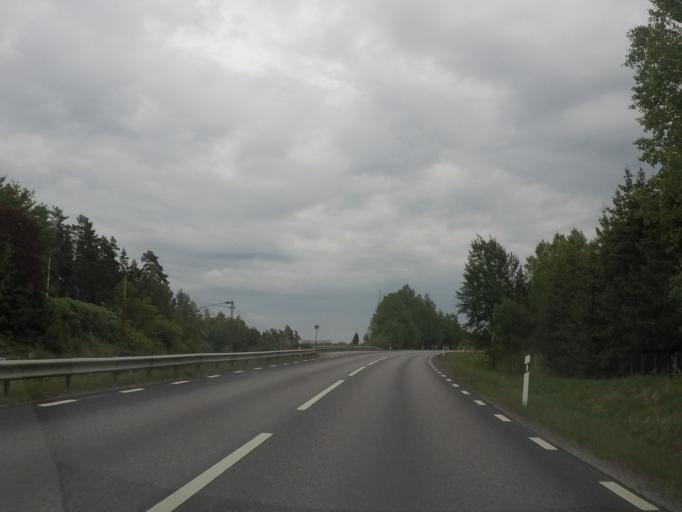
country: SE
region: Soedermanland
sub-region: Flens Kommun
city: Malmkoping
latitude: 59.0679
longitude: 16.7822
